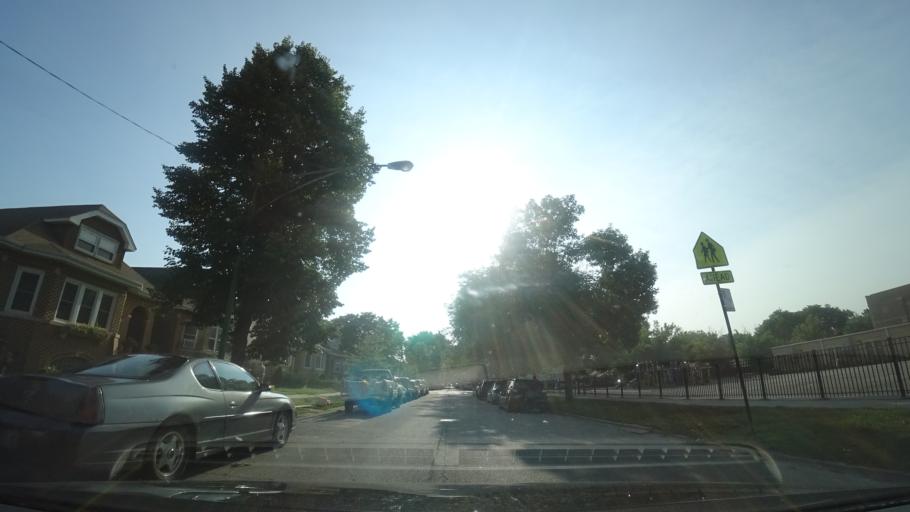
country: US
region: Illinois
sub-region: Cook County
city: Harwood Heights
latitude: 41.9668
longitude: -87.7732
